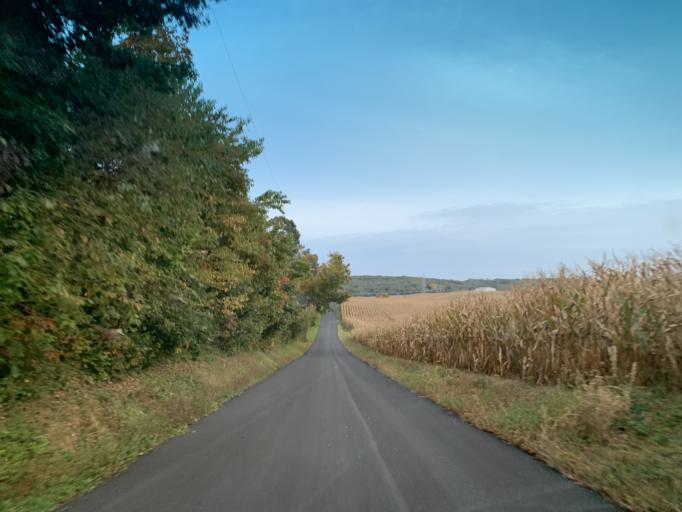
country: US
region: Pennsylvania
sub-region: York County
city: Stewartstown
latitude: 39.6607
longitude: -76.6333
